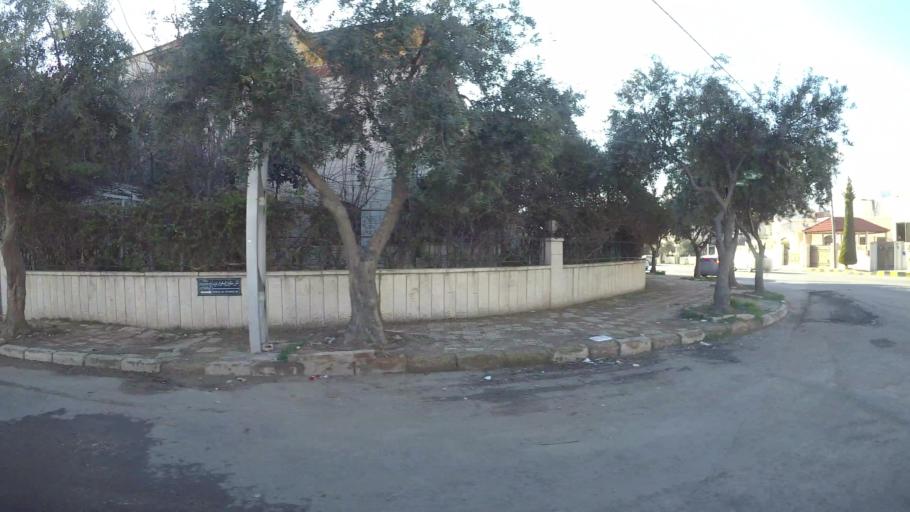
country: JO
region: Amman
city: Al Bunayyat ash Shamaliyah
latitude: 31.8970
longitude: 35.9123
